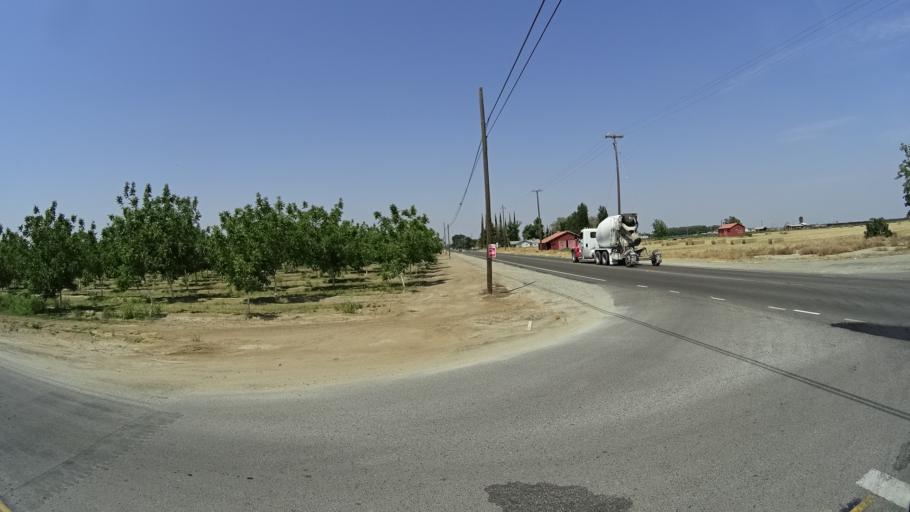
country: US
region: California
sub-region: Kings County
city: Armona
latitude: 36.3134
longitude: -119.7447
